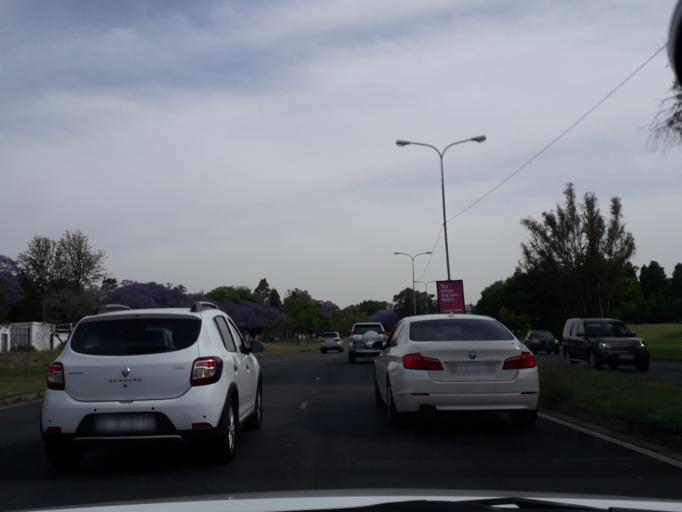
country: ZA
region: Gauteng
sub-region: City of Johannesburg Metropolitan Municipality
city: Johannesburg
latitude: -26.1032
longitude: 28.0326
